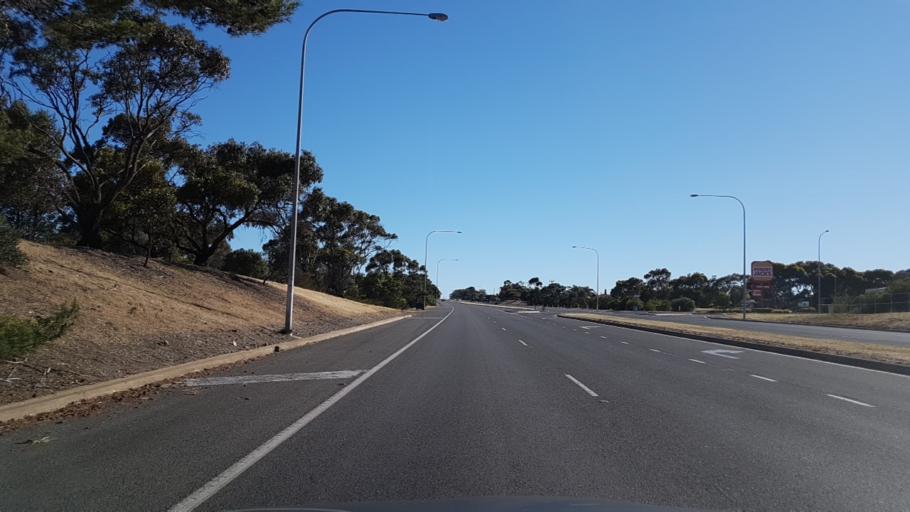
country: AU
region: South Australia
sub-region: Marion
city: Happy Valley
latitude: -35.0757
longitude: 138.5213
